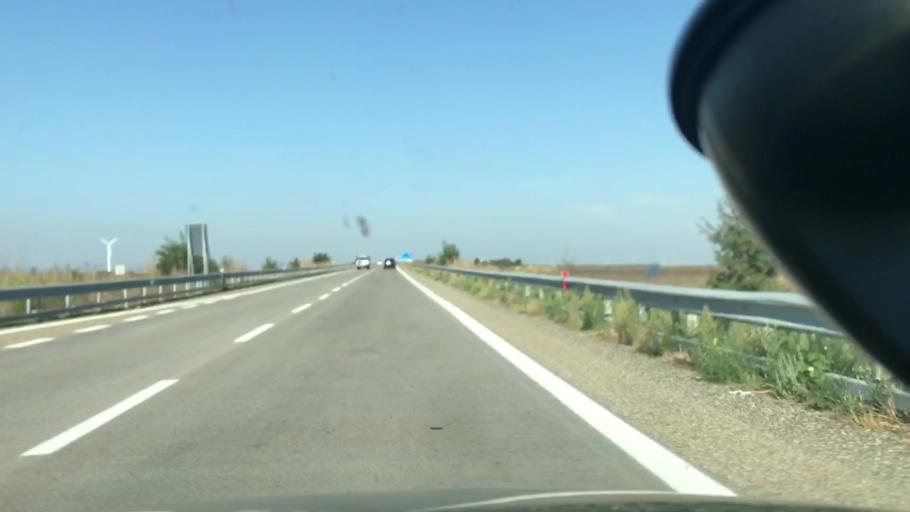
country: IT
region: Basilicate
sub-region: Provincia di Potenza
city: Montemilone
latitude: 40.9904
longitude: 15.8998
